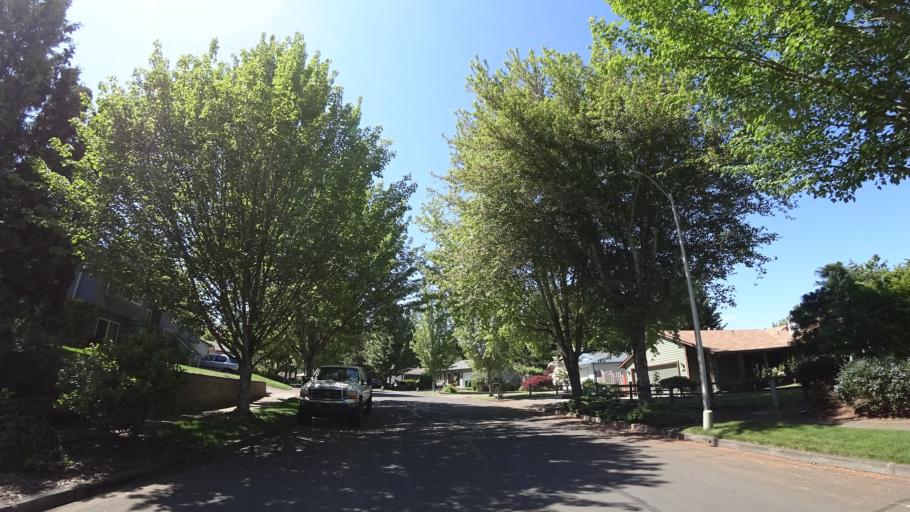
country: US
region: Oregon
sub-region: Washington County
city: Beaverton
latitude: 45.4467
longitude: -122.8119
